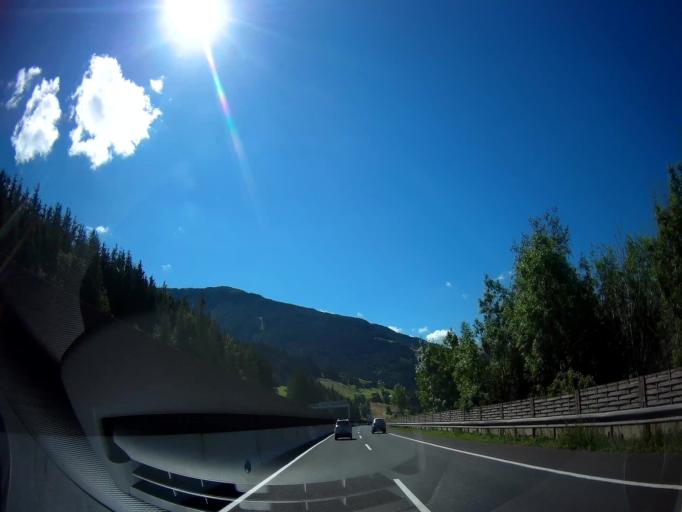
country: AT
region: Salzburg
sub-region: Politischer Bezirk Tamsweg
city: Sankt Michael im Lungau
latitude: 47.0223
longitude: 13.6105
